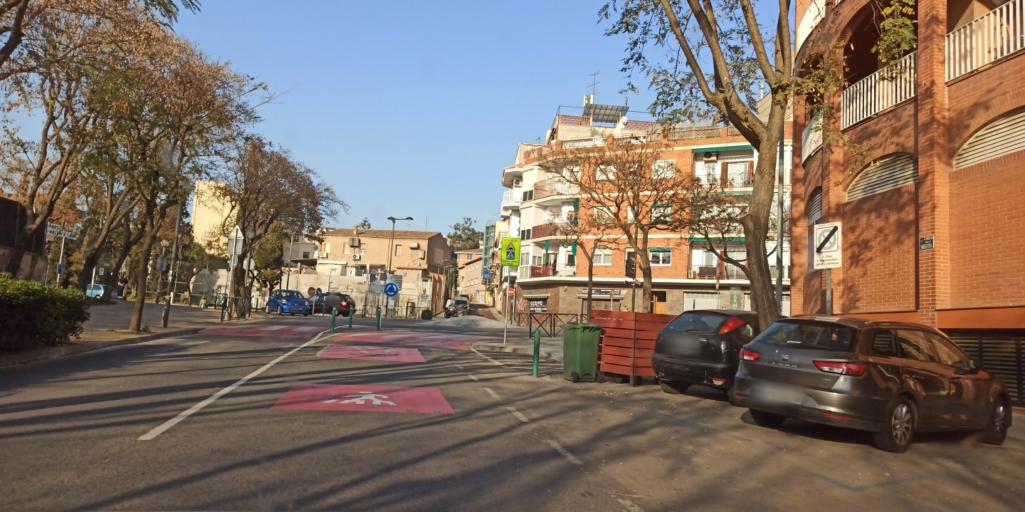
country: ES
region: Catalonia
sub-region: Provincia de Barcelona
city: Sant Just Desvern
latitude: 41.3852
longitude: 2.0732
